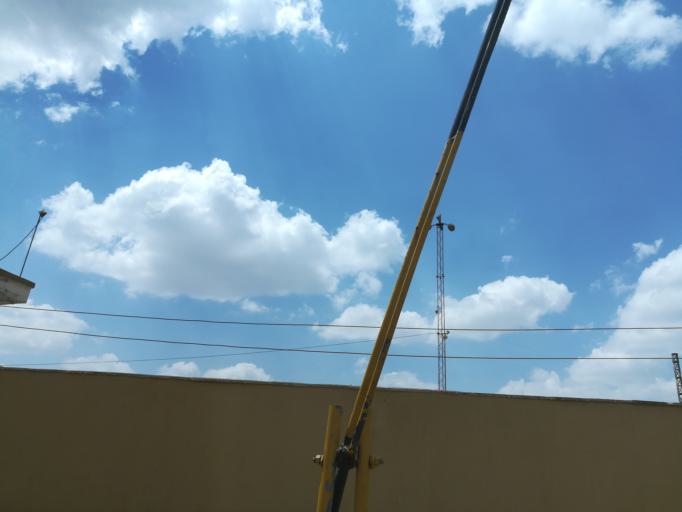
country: KE
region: Nairobi Area
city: Nairobi
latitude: -1.3176
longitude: 36.8145
